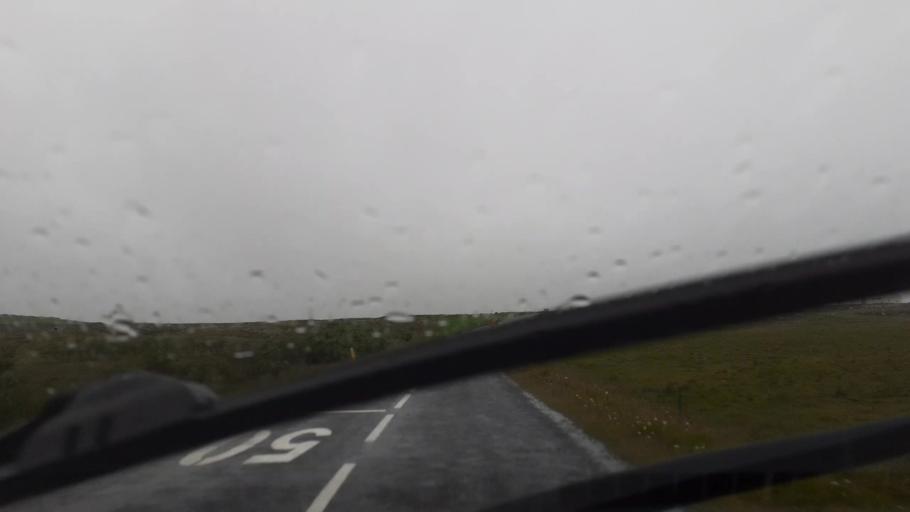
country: IS
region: Northeast
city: Husavik
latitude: 66.4584
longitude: -15.9517
